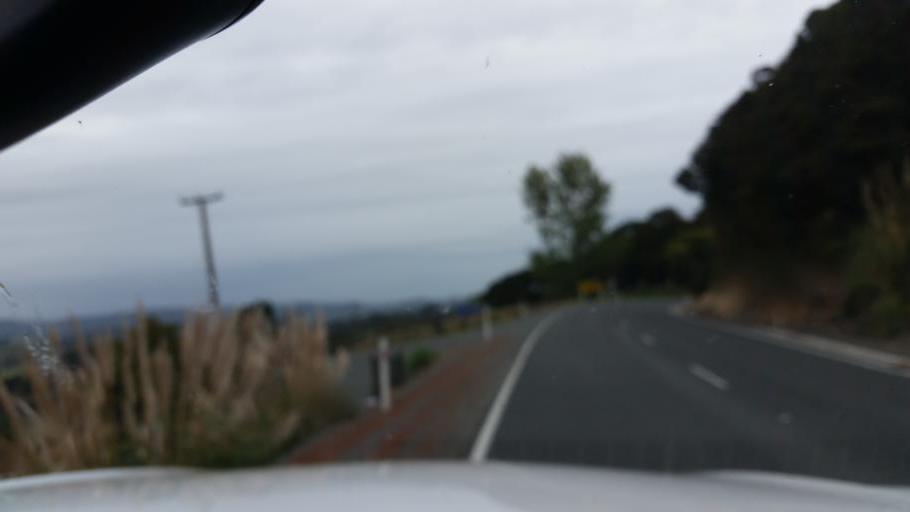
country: NZ
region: Auckland
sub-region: Auckland
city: Wellsford
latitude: -36.1628
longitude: 174.5825
